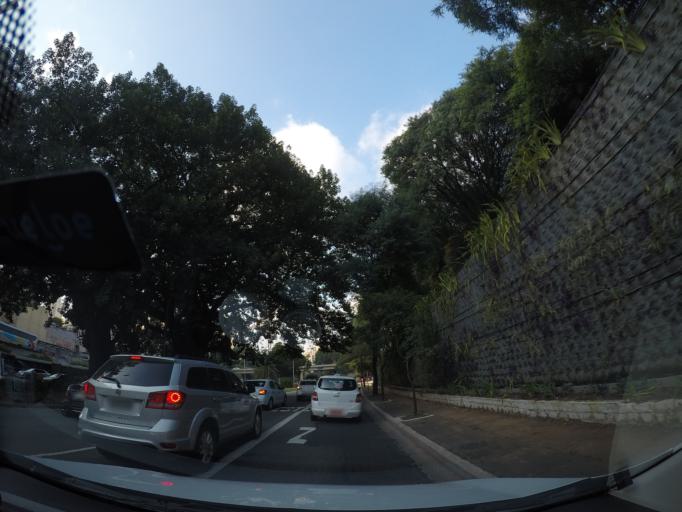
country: BR
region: Sao Paulo
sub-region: Sao Paulo
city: Sao Paulo
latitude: -23.5613
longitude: -46.6376
